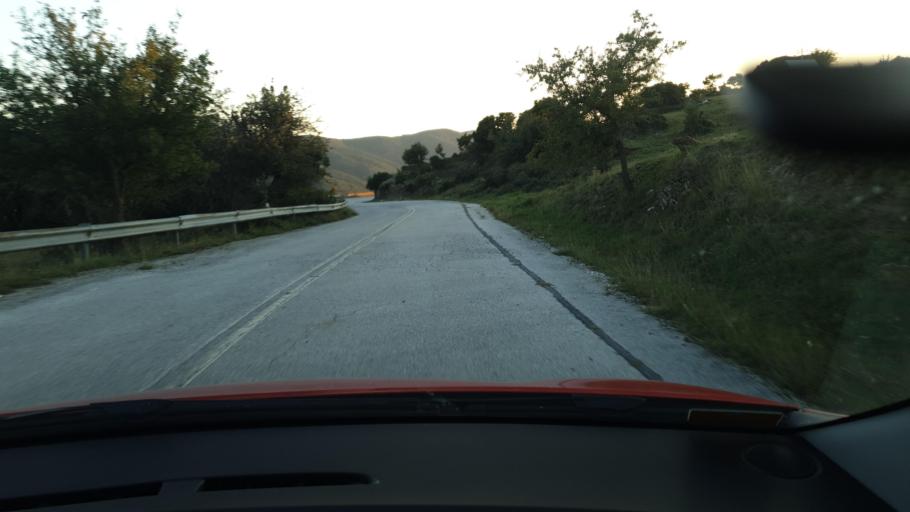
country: GR
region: Central Macedonia
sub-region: Nomos Chalkidikis
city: Galatista
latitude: 40.4572
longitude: 23.3175
